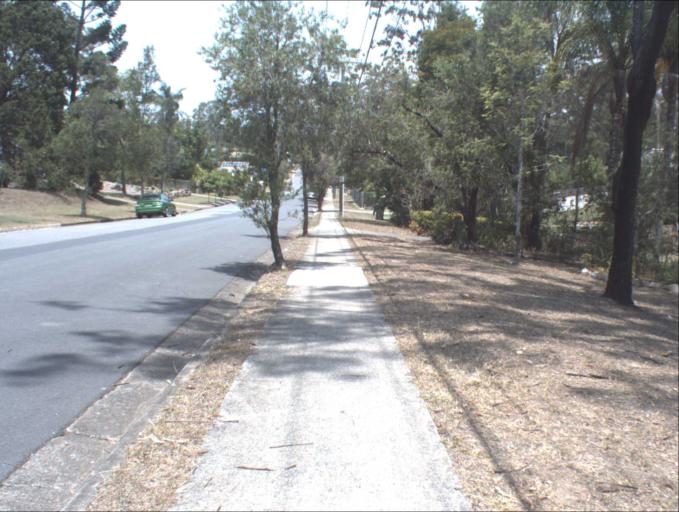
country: AU
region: Queensland
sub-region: Logan
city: Beenleigh
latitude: -27.6676
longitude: 153.1979
